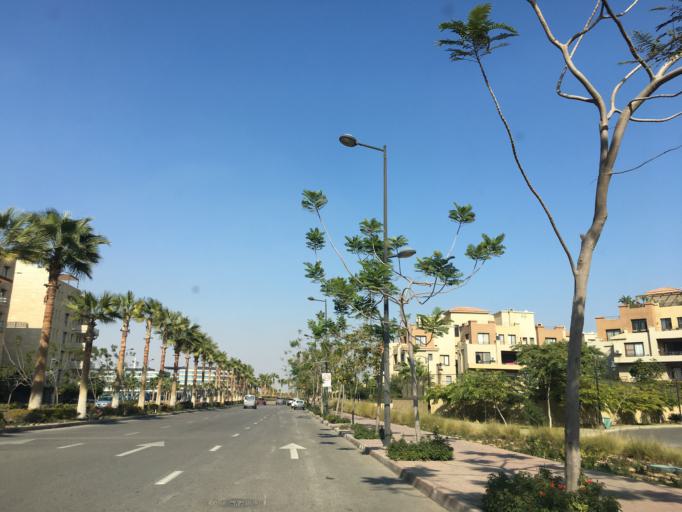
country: EG
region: Al Jizah
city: Awsim
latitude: 30.0661
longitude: 30.9469
